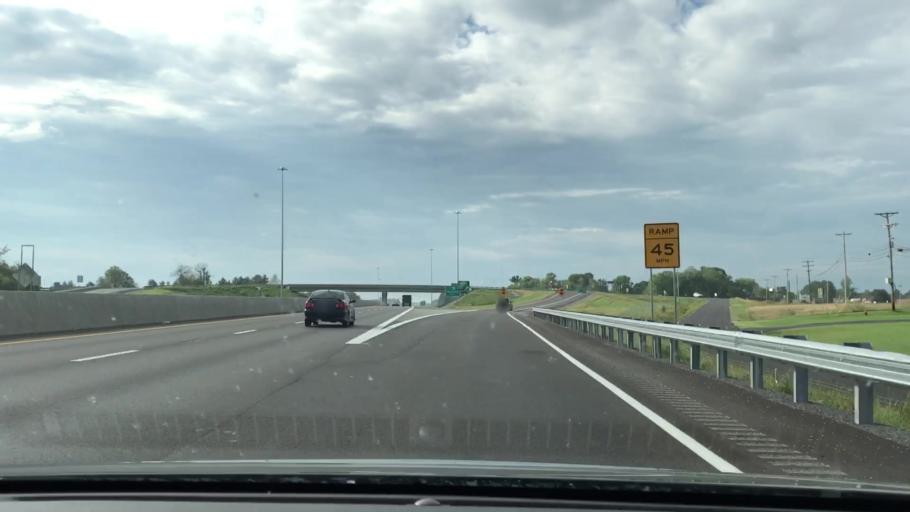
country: US
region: Kentucky
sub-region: Graves County
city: Mayfield
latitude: 36.7418
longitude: -88.6677
